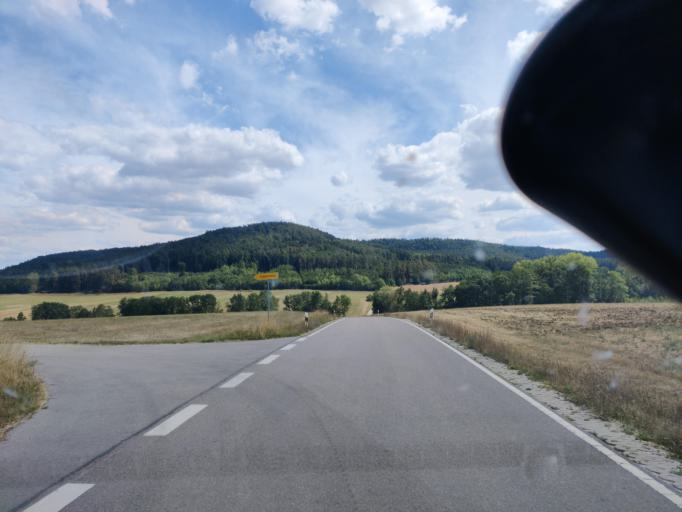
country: DE
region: Bavaria
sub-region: Regierungsbezirk Mittelfranken
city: Bergen
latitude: 49.0959
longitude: 11.1430
